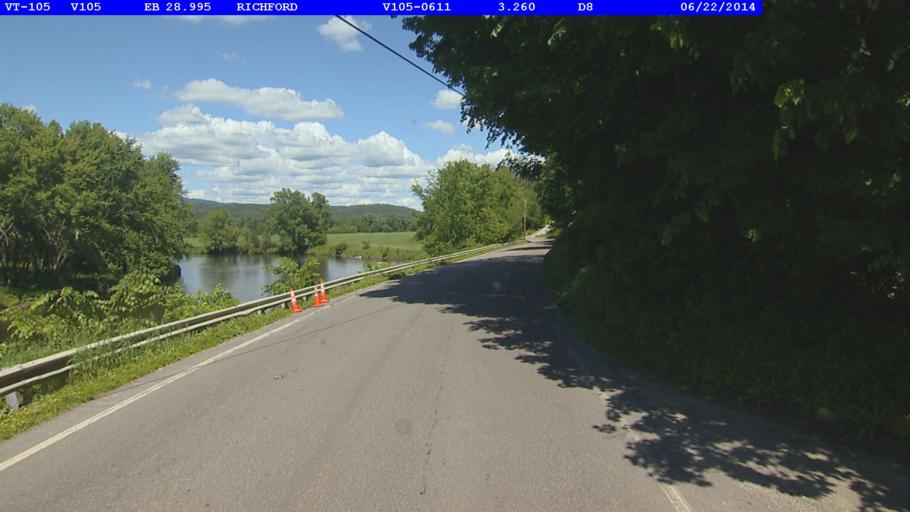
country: US
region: Vermont
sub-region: Franklin County
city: Richford
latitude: 44.9871
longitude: -72.6532
